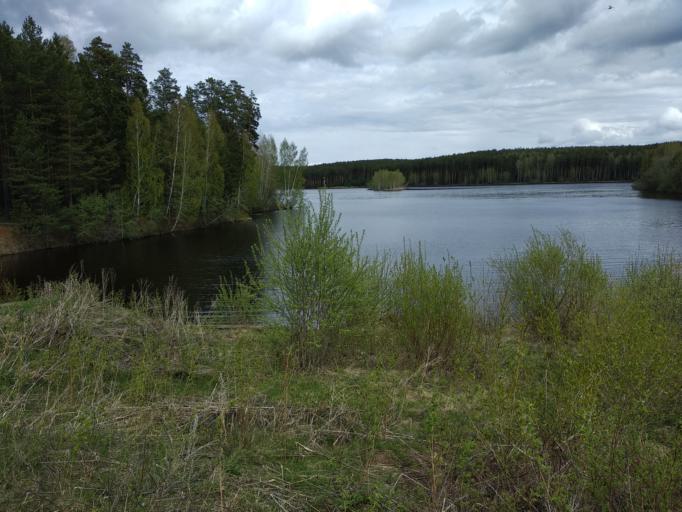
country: RU
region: Sverdlovsk
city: Staropyshminsk
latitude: 56.9210
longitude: 60.8560
